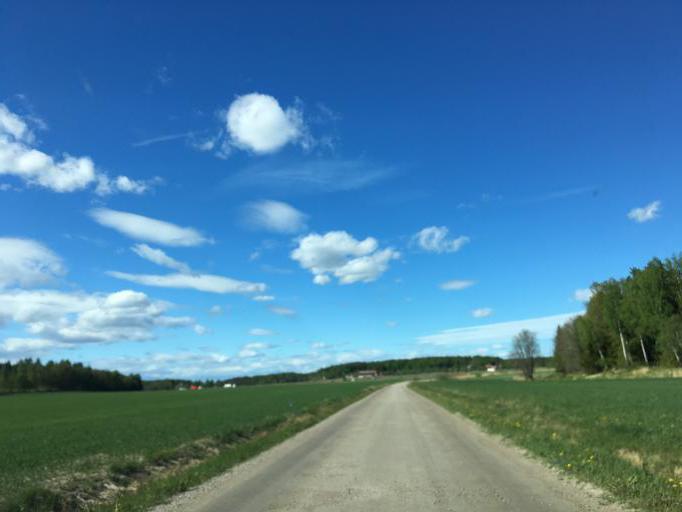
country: SE
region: Soedermanland
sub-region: Eskilstuna Kommun
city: Kvicksund
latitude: 59.4016
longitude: 16.2387
